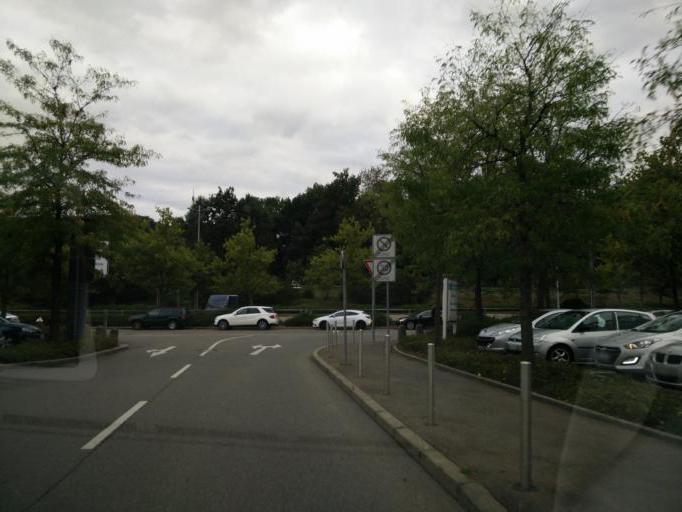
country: DE
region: Baden-Wuerttemberg
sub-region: Regierungsbezirk Stuttgart
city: Sindelfingen
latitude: 48.7036
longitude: 9.0326
